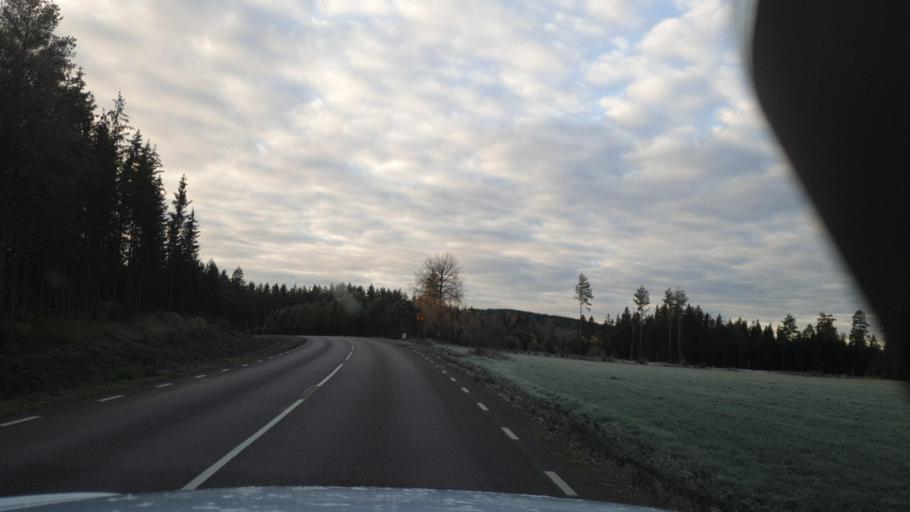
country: SE
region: Vaermland
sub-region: Eda Kommun
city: Amotfors
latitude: 59.7328
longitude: 12.1698
